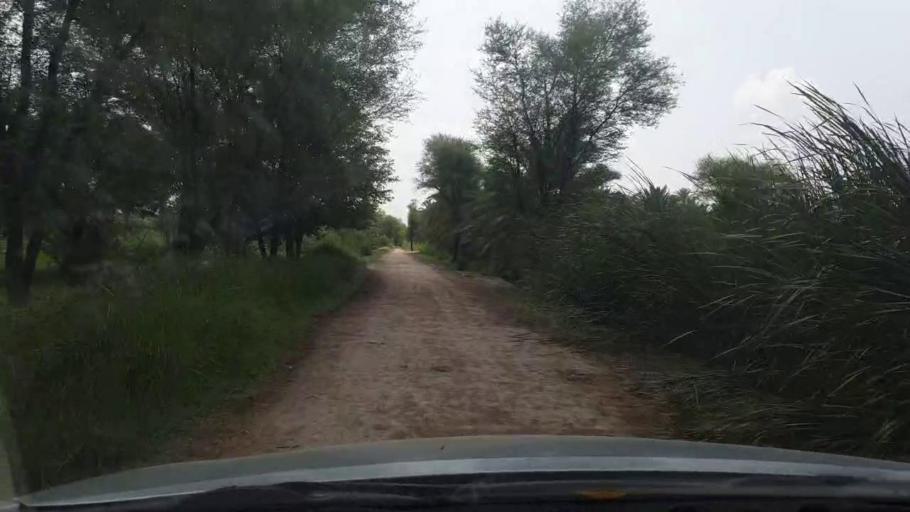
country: PK
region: Sindh
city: Khairpur
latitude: 27.4852
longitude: 68.7302
